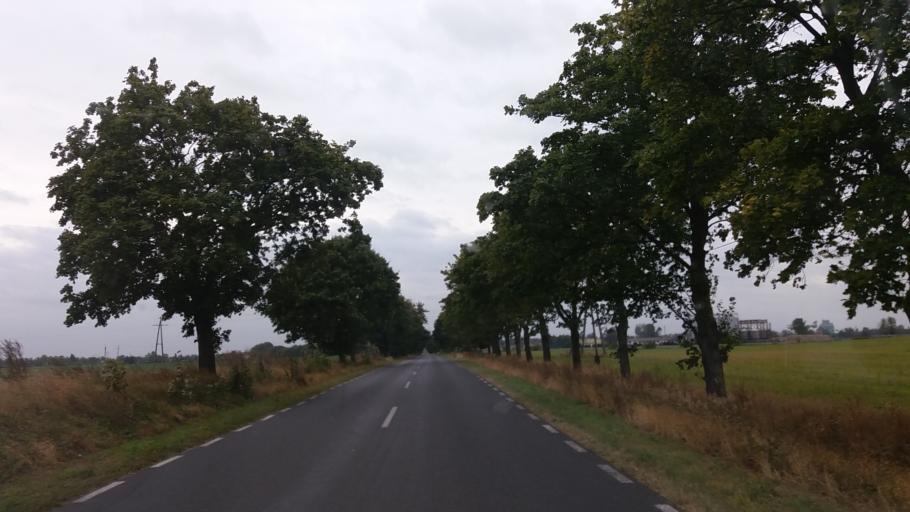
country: PL
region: Lubusz
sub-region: Powiat strzelecko-drezdenecki
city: Strzelce Krajenskie
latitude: 52.8936
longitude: 15.5436
